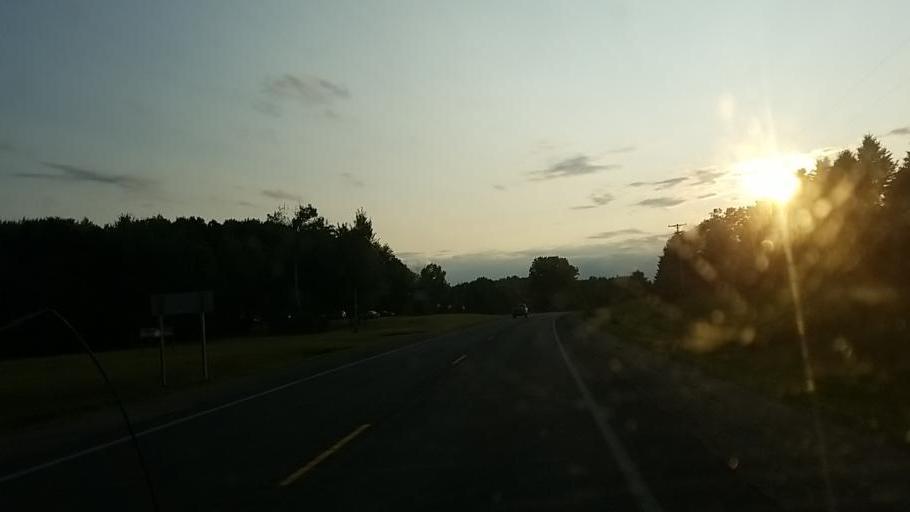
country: US
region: Michigan
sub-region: Newaygo County
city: Newaygo
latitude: 43.3967
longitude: -85.6445
